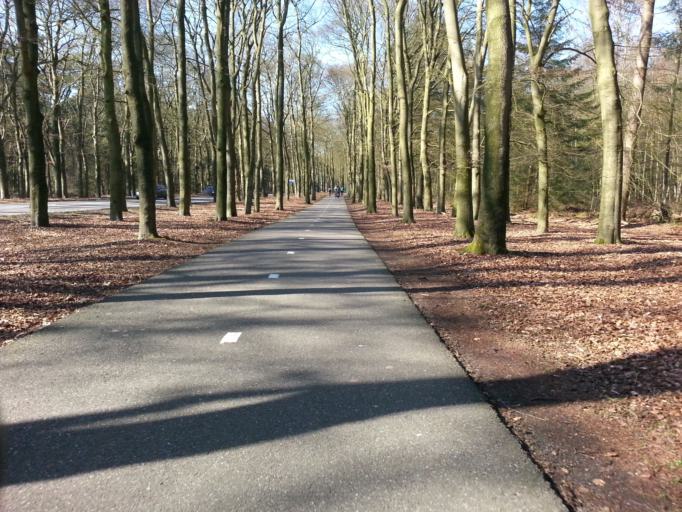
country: NL
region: Utrecht
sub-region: Gemeente Utrechtse Heuvelrug
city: Doorn
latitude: 52.0311
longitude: 5.3753
